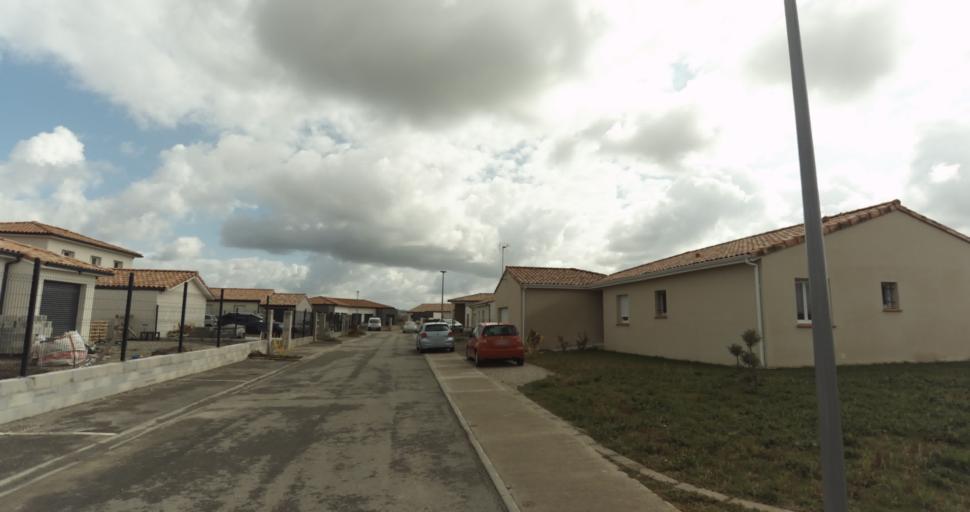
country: FR
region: Midi-Pyrenees
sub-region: Departement de la Haute-Garonne
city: Auterive
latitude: 43.3431
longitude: 1.4570
